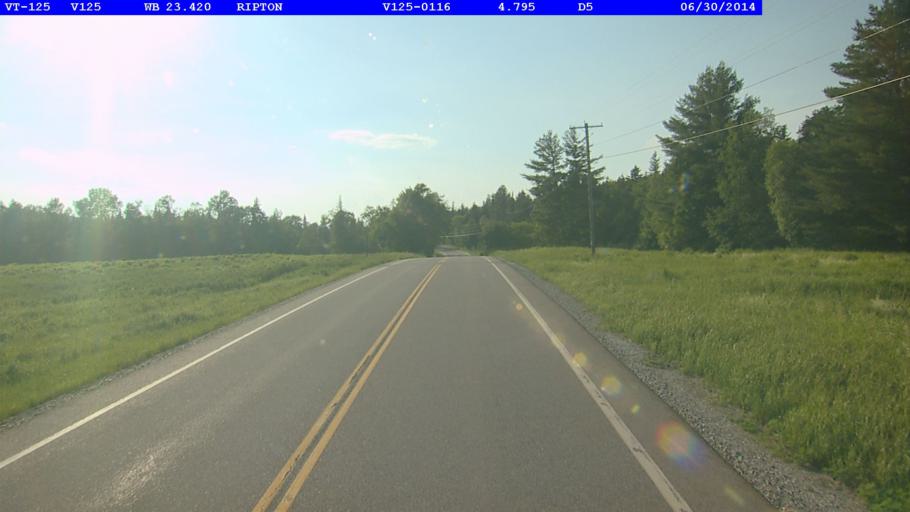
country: US
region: Vermont
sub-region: Rutland County
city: Brandon
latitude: 43.9492
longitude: -72.9839
